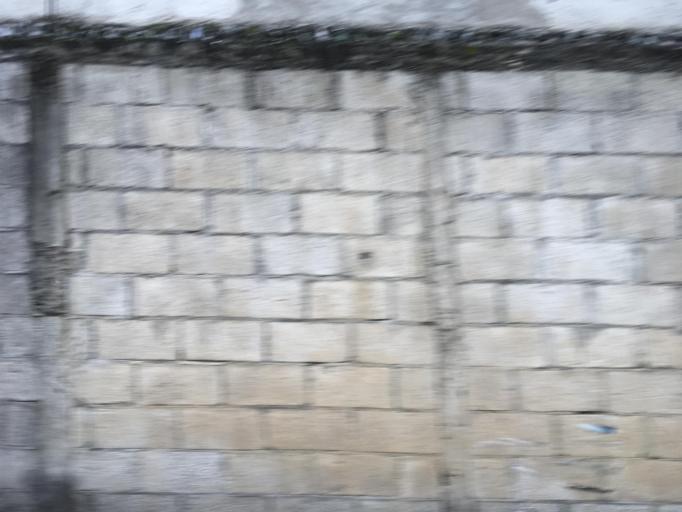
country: GT
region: Sacatepequez
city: Jocotenango
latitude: 14.5756
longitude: -90.7454
